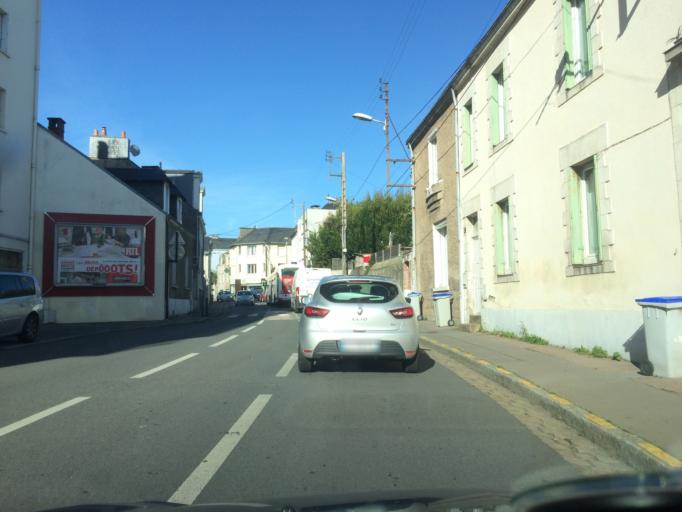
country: FR
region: Pays de la Loire
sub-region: Departement de la Loire-Atlantique
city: Nantes
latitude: 47.2338
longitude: -1.5418
